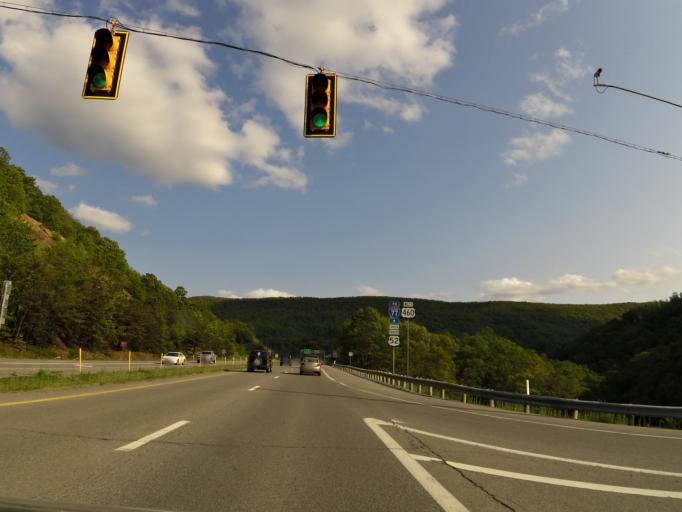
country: US
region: West Virginia
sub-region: Mercer County
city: Bluefield
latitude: 37.2827
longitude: -81.1676
